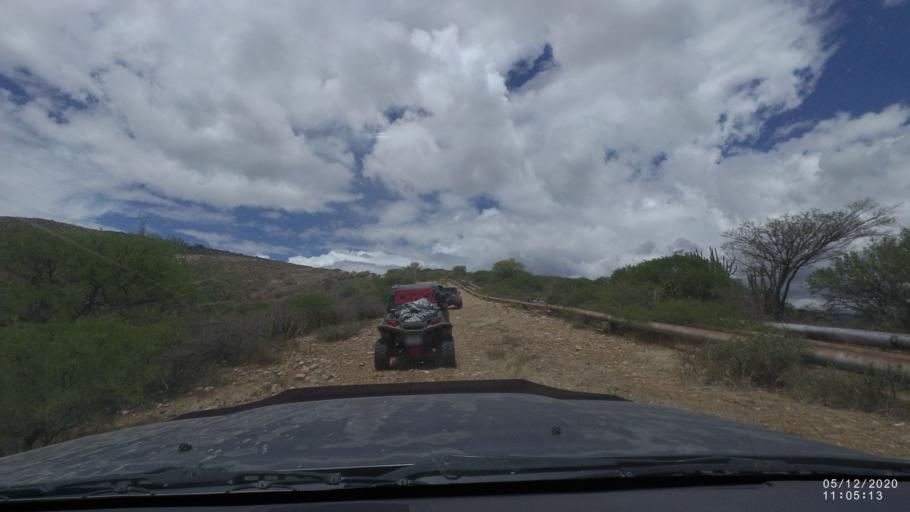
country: BO
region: Cochabamba
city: Sipe Sipe
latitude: -17.5494
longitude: -66.3031
